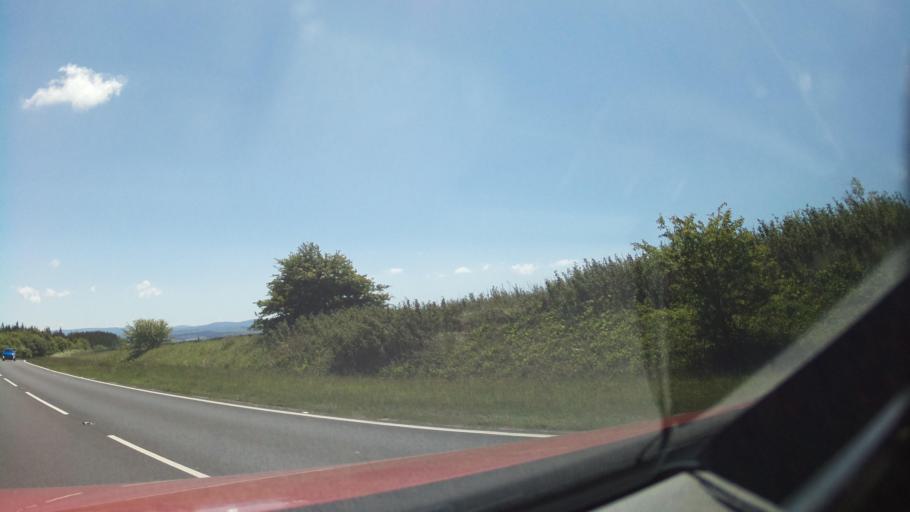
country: GB
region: Scotland
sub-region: The Scottish Borders
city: Hawick
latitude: 55.4726
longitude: -2.7952
